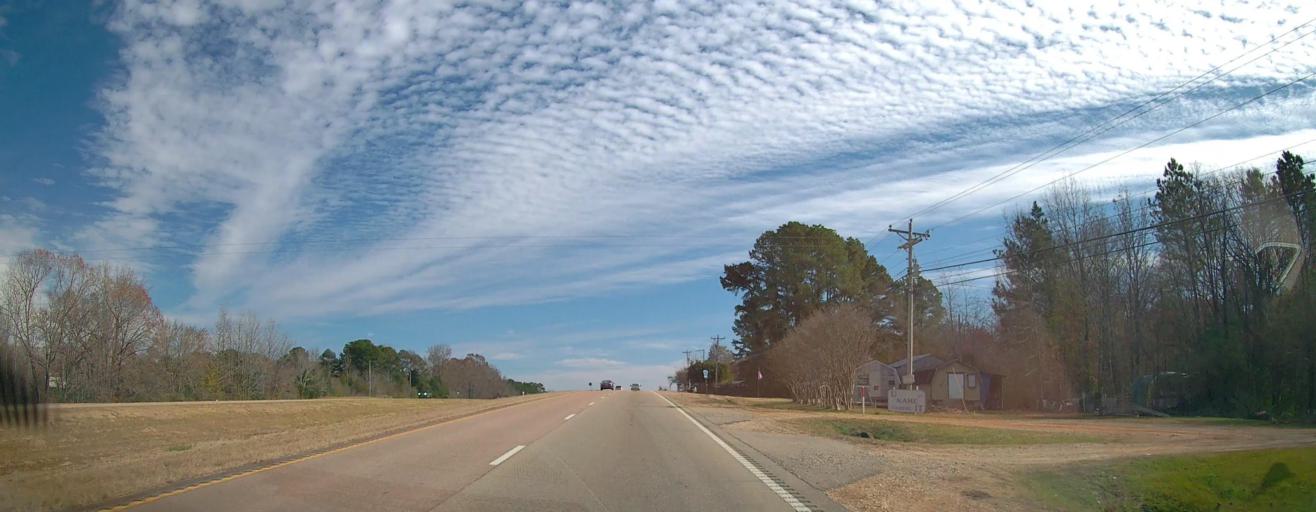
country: US
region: Mississippi
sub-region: Tippah County
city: Ripley
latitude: 34.9543
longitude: -88.8435
